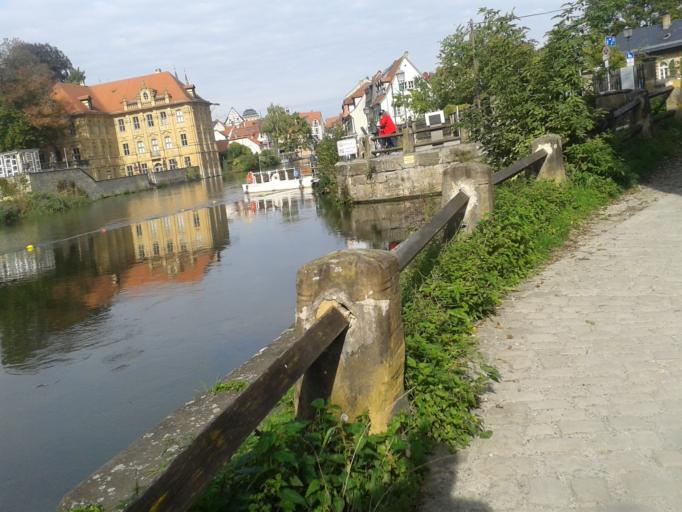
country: DE
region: Bavaria
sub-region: Upper Franconia
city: Bamberg
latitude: 49.8873
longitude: 10.8903
